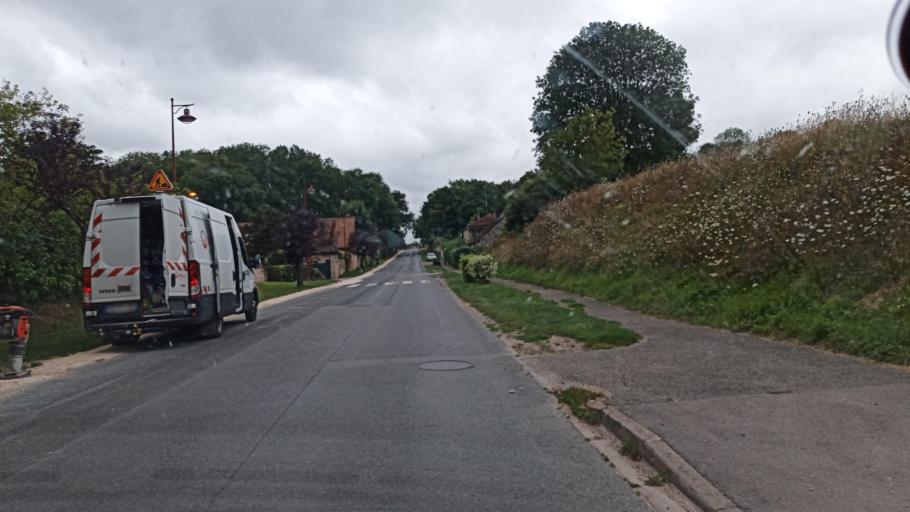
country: FR
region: Ile-de-France
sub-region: Departement de Seine-et-Marne
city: Voulx
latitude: 48.2844
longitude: 2.9668
